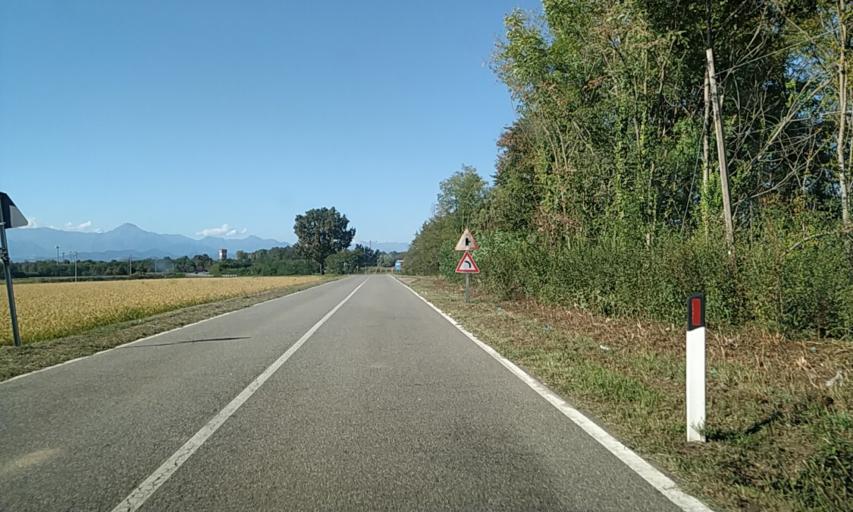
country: IT
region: Piedmont
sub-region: Provincia di Vercelli
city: Rovasenda
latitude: 45.5246
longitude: 8.3194
